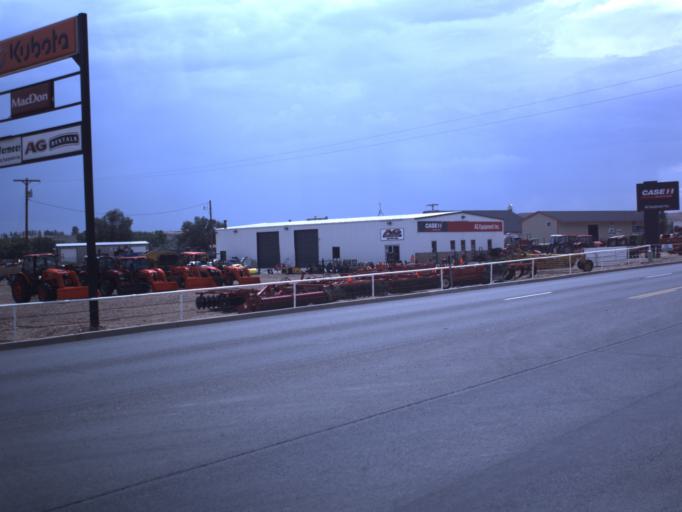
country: US
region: Utah
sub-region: Duchesne County
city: Roosevelt
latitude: 40.2758
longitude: -110.0258
